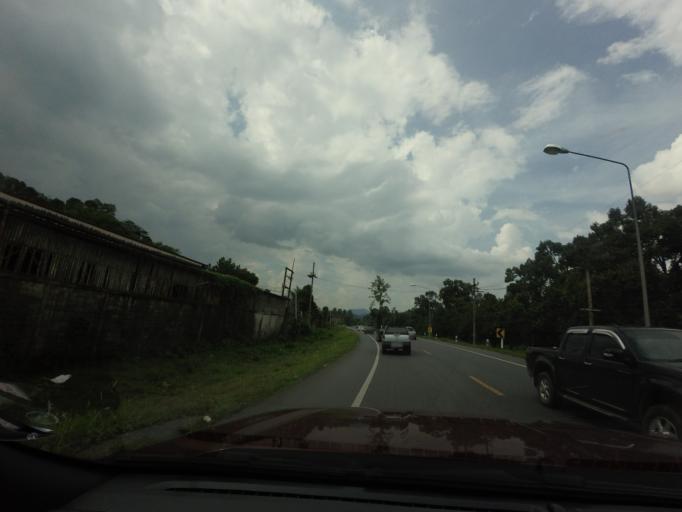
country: TH
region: Yala
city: Ban Nang Sata
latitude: 6.2650
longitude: 101.2769
